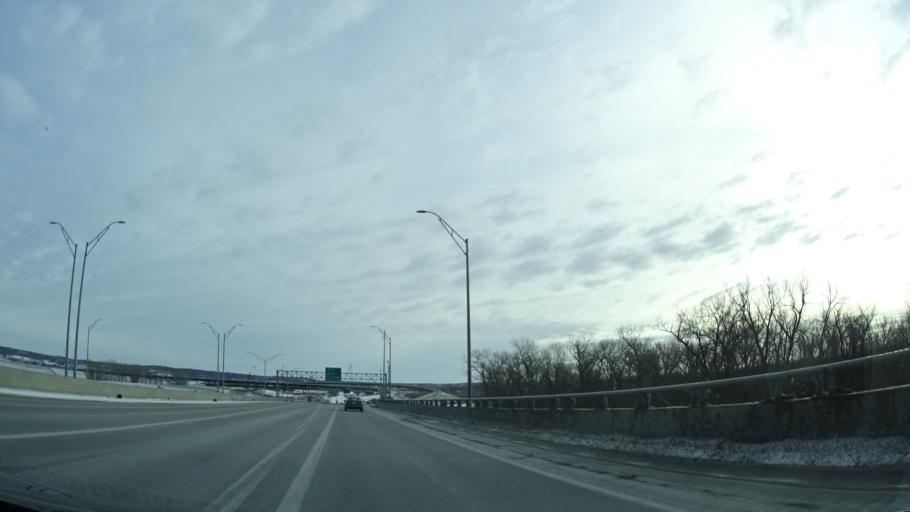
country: US
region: Nebraska
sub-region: Douglas County
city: Omaha
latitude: 41.2317
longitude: -95.9084
